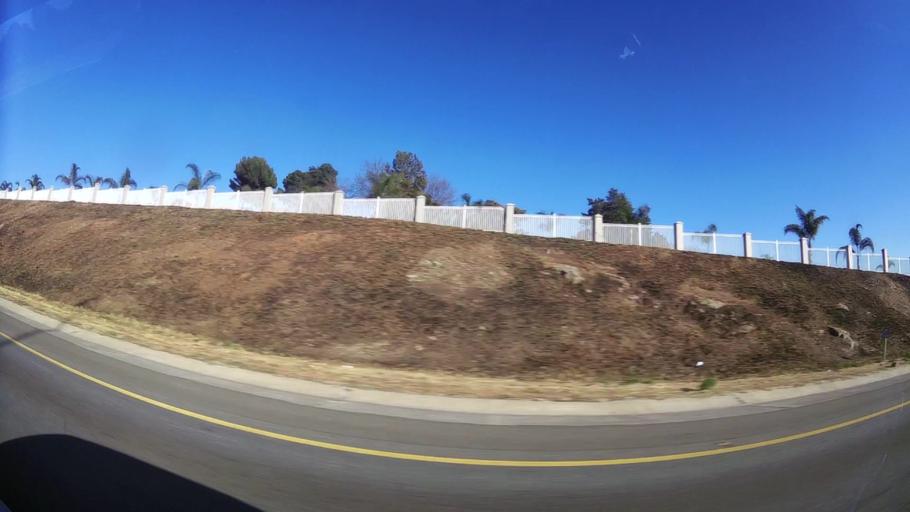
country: ZA
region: Gauteng
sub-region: City of Tshwane Metropolitan Municipality
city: Centurion
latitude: -25.8924
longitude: 28.2546
